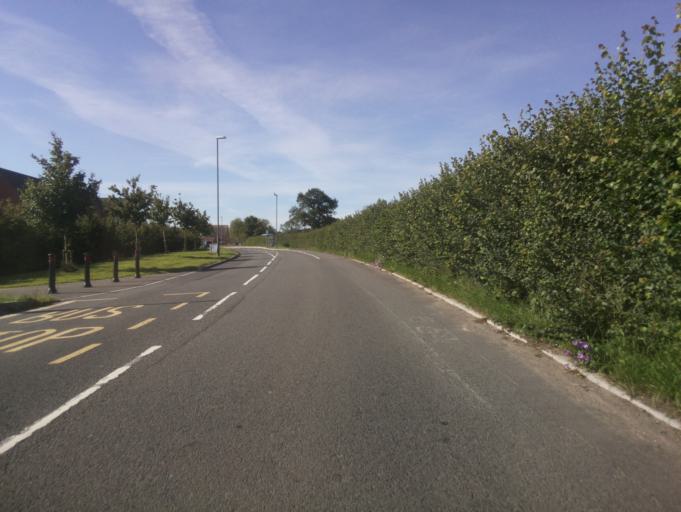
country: GB
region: England
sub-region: Bath and North East Somerset
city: Keynsham
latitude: 51.4051
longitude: -2.5166
